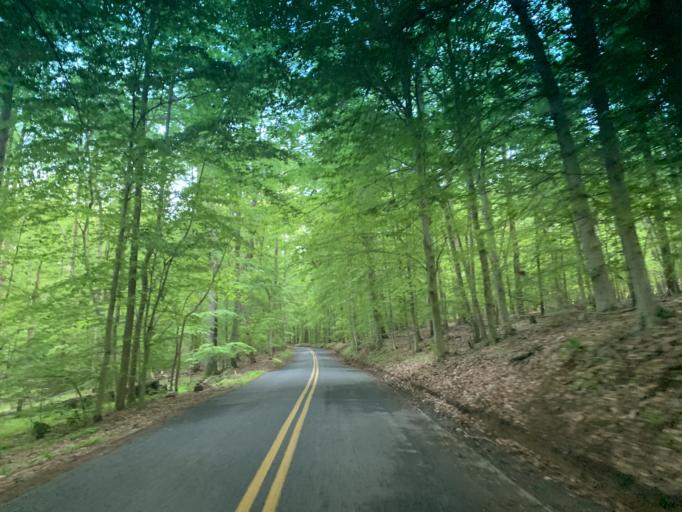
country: US
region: Pennsylvania
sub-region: York County
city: Susquehanna Trails
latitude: 39.6921
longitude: -76.2421
